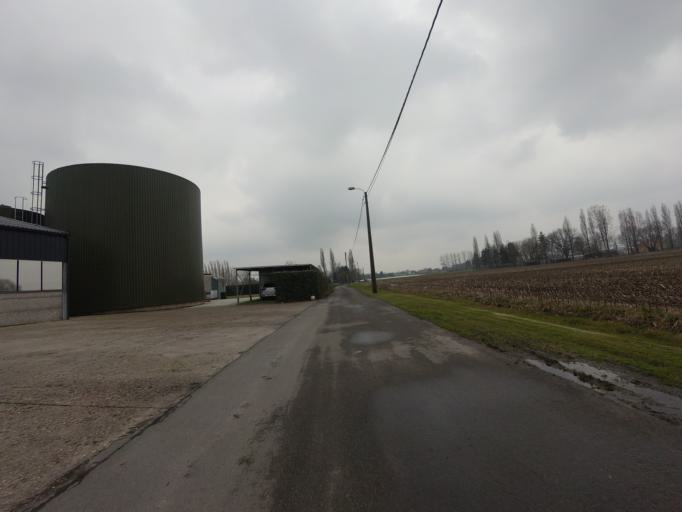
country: BE
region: Flanders
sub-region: Provincie Antwerpen
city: Putte
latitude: 51.0692
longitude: 4.5997
